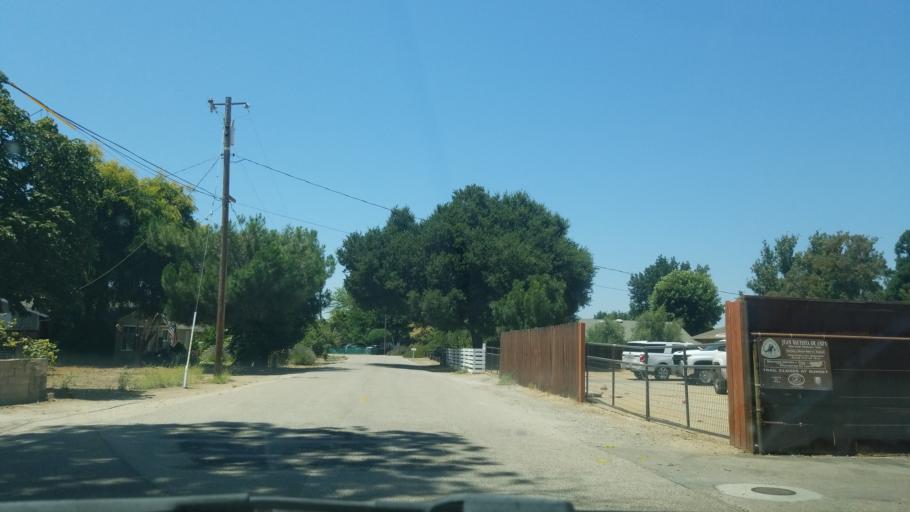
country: US
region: California
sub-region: San Luis Obispo County
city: Atascadero
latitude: 35.5084
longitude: -120.6638
